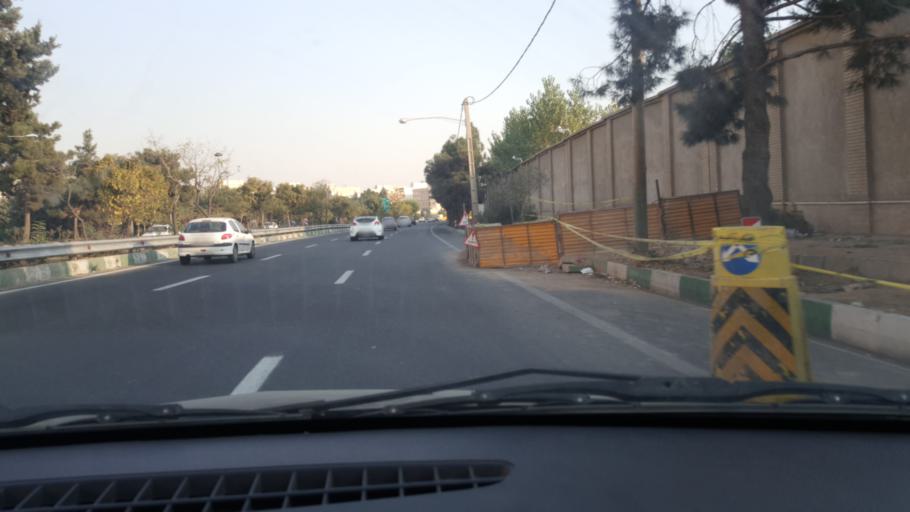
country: IR
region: Tehran
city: Tehran
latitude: 35.7389
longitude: 51.2809
